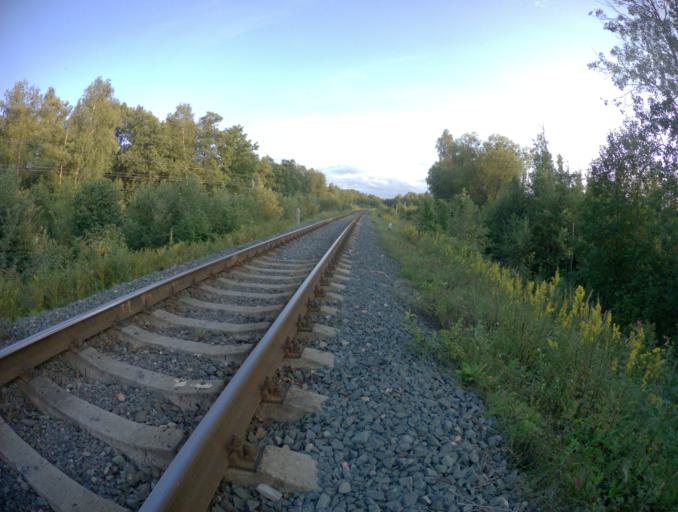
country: RU
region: Vladimir
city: Raduzhnyy
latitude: 56.0399
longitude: 40.3848
